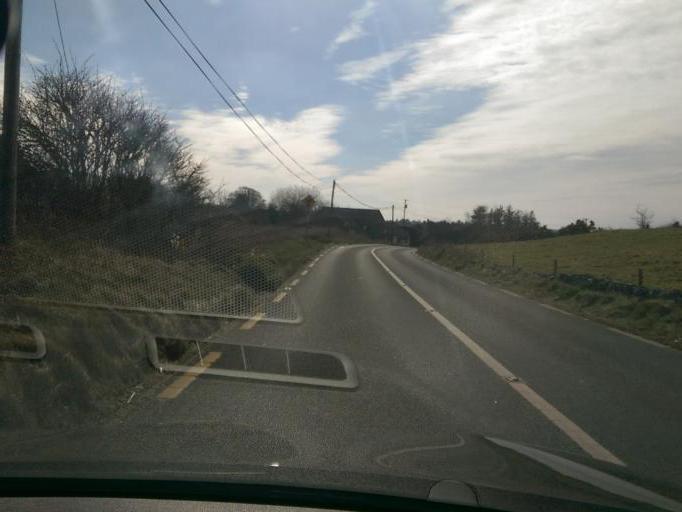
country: IE
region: Connaught
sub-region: County Galway
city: Athenry
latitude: 53.4629
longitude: -8.6707
